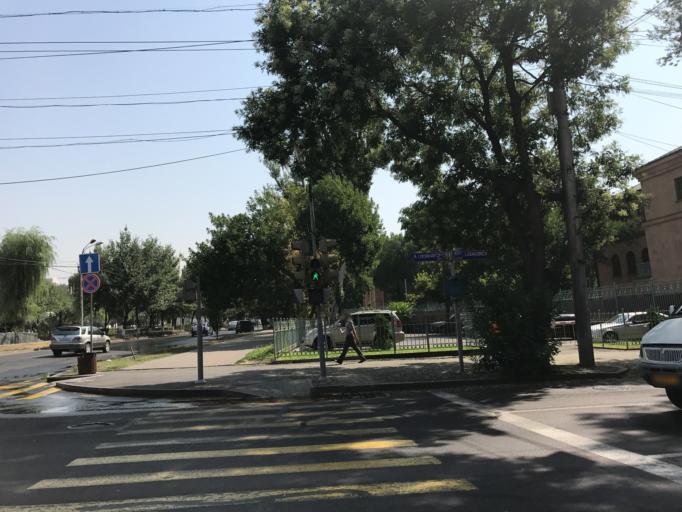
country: AM
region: Yerevan
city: Yerevan
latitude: 40.1742
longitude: 44.5059
